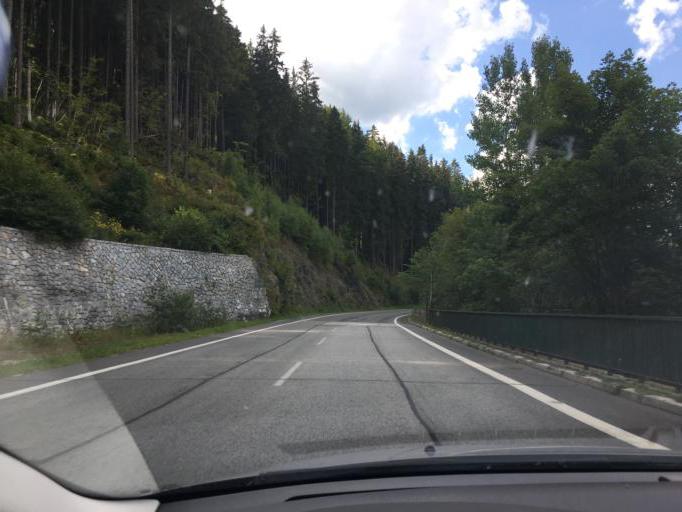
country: CZ
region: Kralovehradecky
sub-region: Okres Trutnov
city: Spindleruv Mlyn
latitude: 50.7061
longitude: 15.5828
